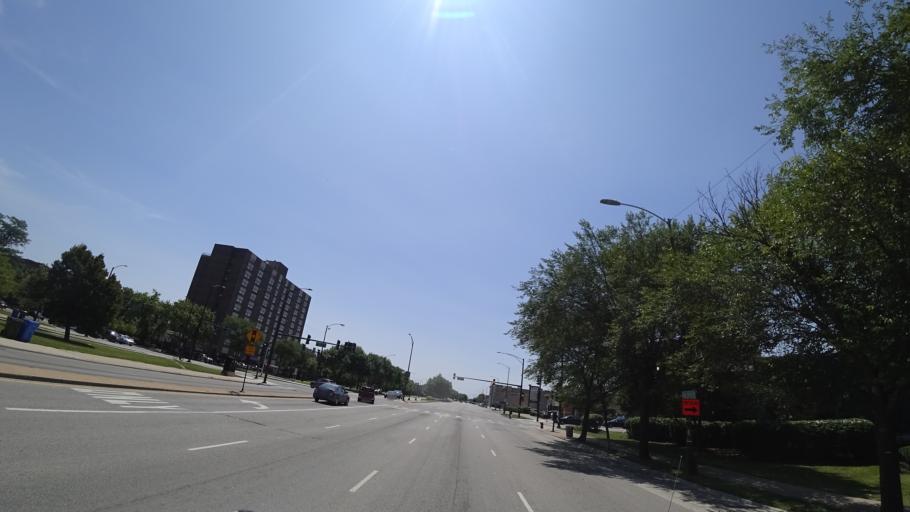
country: US
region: Illinois
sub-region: Cook County
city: Chicago
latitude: 41.7738
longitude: -87.5863
